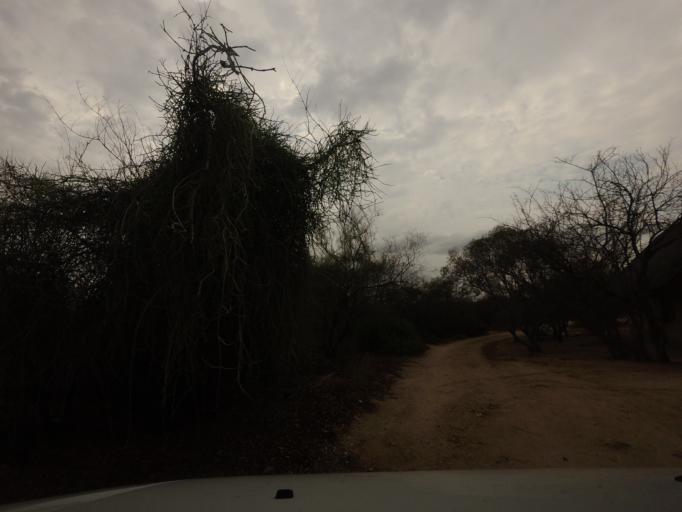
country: ZA
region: Limpopo
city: Thulamahashi
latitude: -24.4743
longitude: 31.3909
